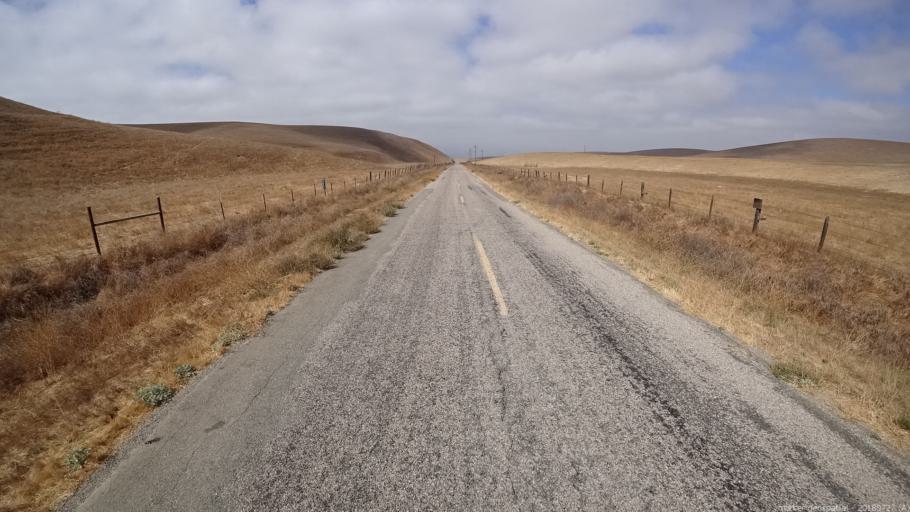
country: US
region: California
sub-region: Monterey County
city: King City
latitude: 36.2305
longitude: -121.0524
